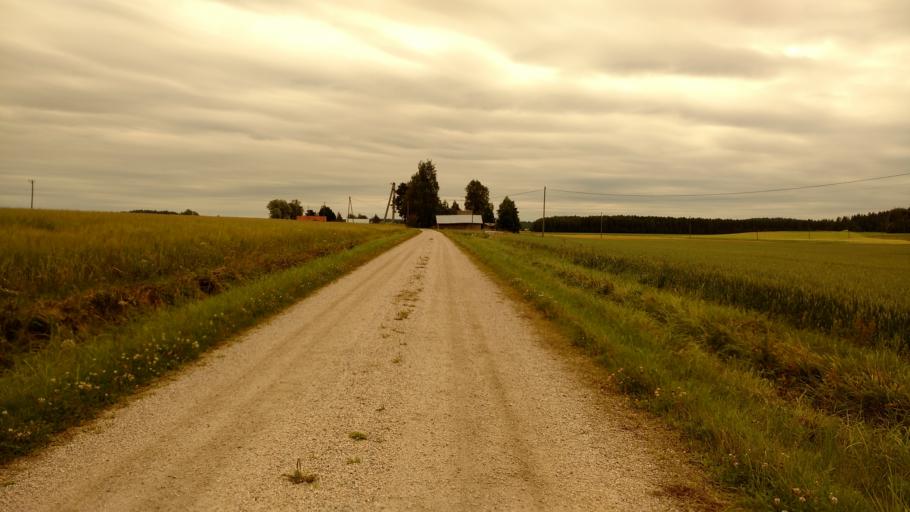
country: FI
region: Varsinais-Suomi
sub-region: Turku
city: Paimio
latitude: 60.4170
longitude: 22.8382
